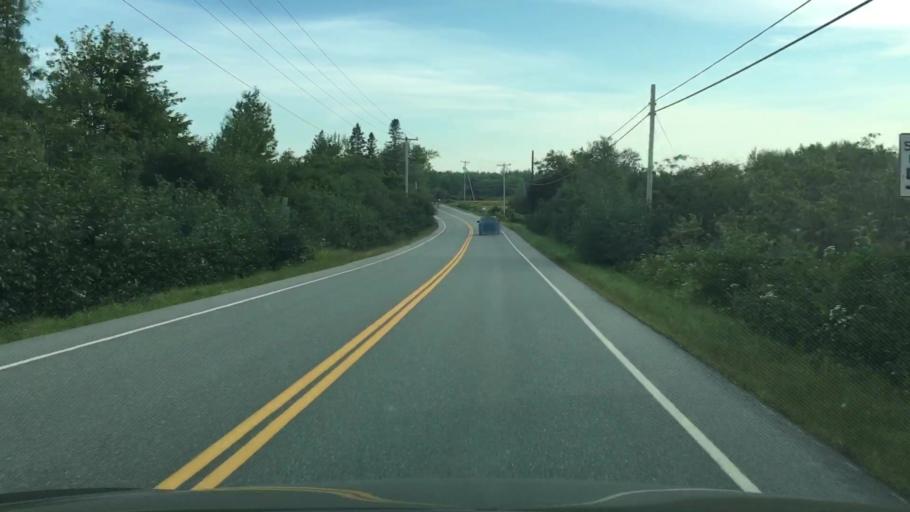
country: US
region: Maine
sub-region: Hancock County
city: Penobscot
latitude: 44.4735
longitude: -68.7801
